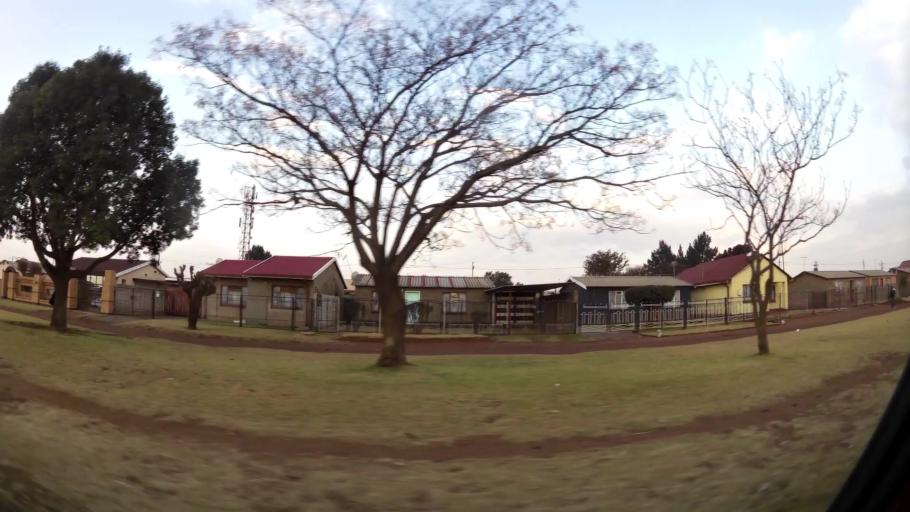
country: ZA
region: Gauteng
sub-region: City of Johannesburg Metropolitan Municipality
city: Orange Farm
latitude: -26.5597
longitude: 27.8383
